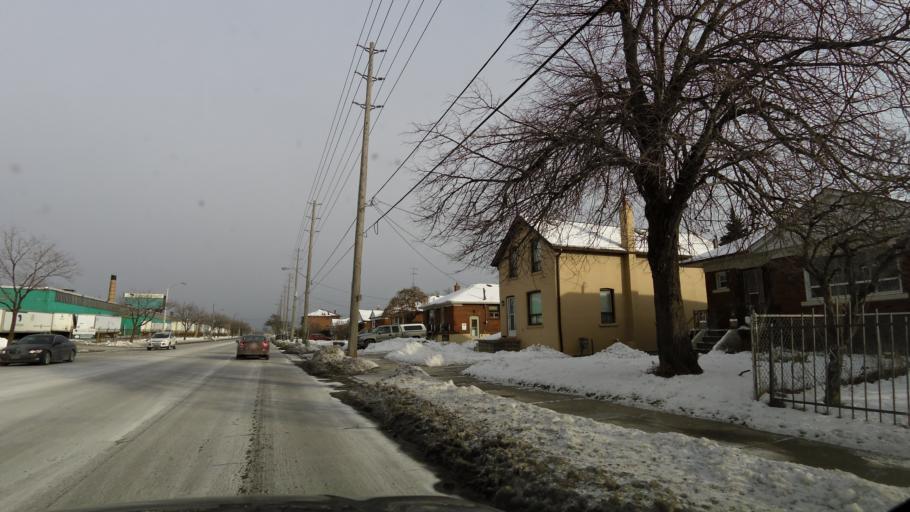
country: CA
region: Ontario
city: Etobicoke
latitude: 43.6138
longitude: -79.5350
